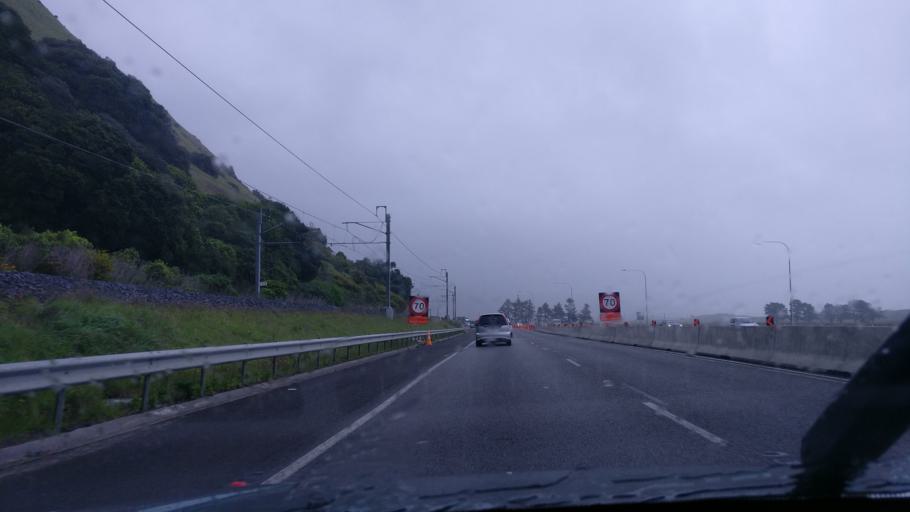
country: NZ
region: Wellington
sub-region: Kapiti Coast District
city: Paraparaumu
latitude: -40.9425
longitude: 174.9924
